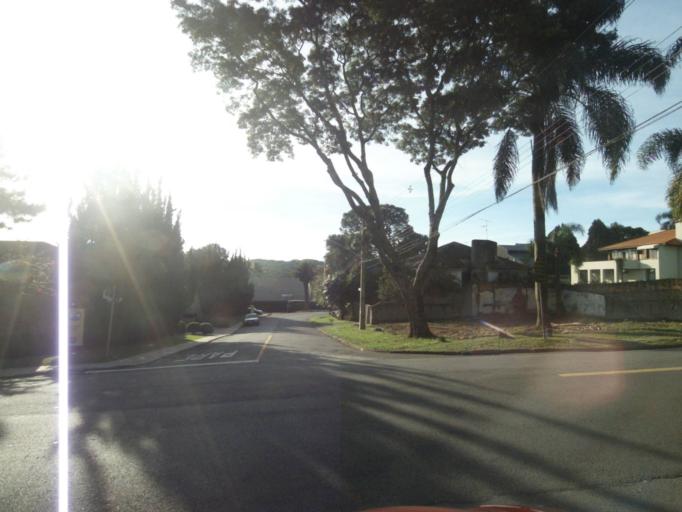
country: BR
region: Parana
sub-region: Curitiba
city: Curitiba
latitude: -25.4315
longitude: -49.3067
